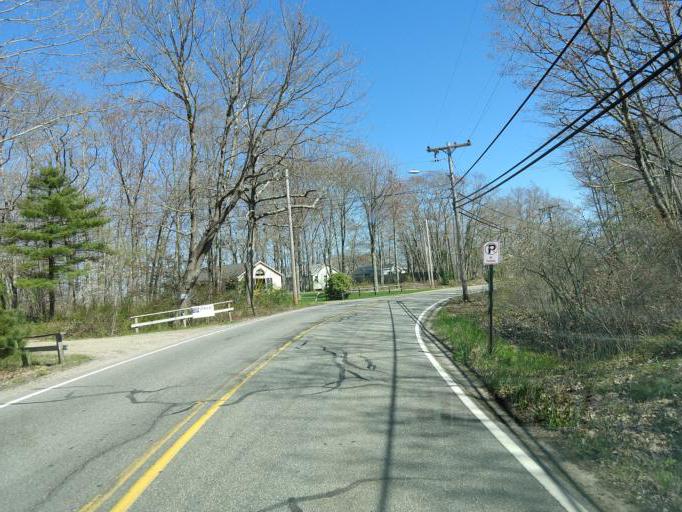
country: US
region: Maine
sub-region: York County
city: Old Orchard Beach
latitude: 43.4387
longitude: -70.3735
